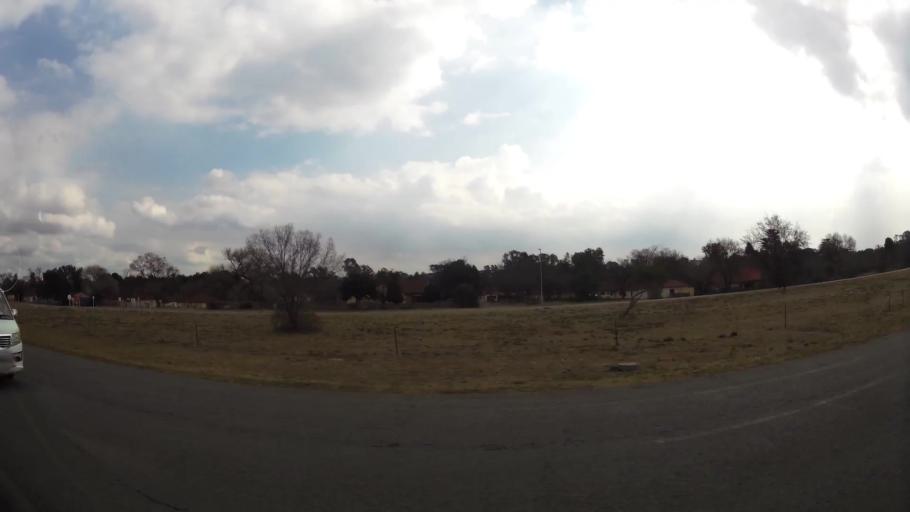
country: ZA
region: Gauteng
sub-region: Sedibeng District Municipality
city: Vereeniging
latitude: -26.6925
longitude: 27.9392
